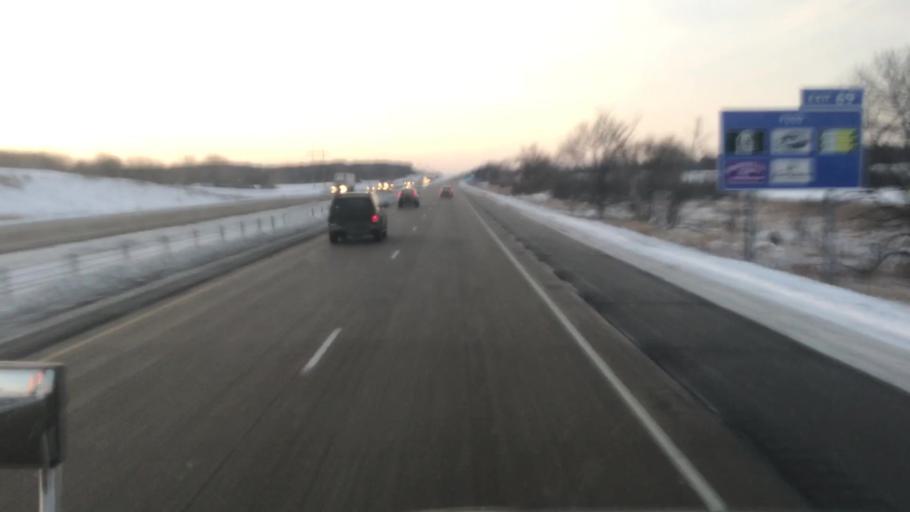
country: US
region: Minnesota
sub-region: Scott County
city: Elko New Market
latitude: 44.4833
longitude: -93.2921
